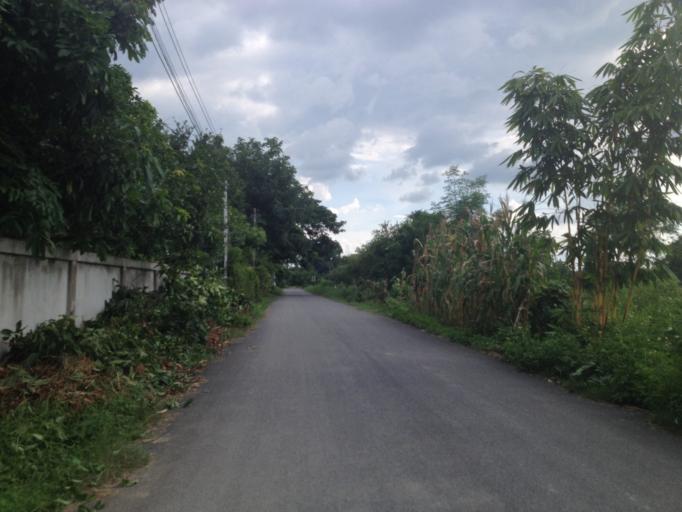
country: TH
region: Chiang Mai
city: Hang Dong
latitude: 18.7175
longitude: 98.9310
